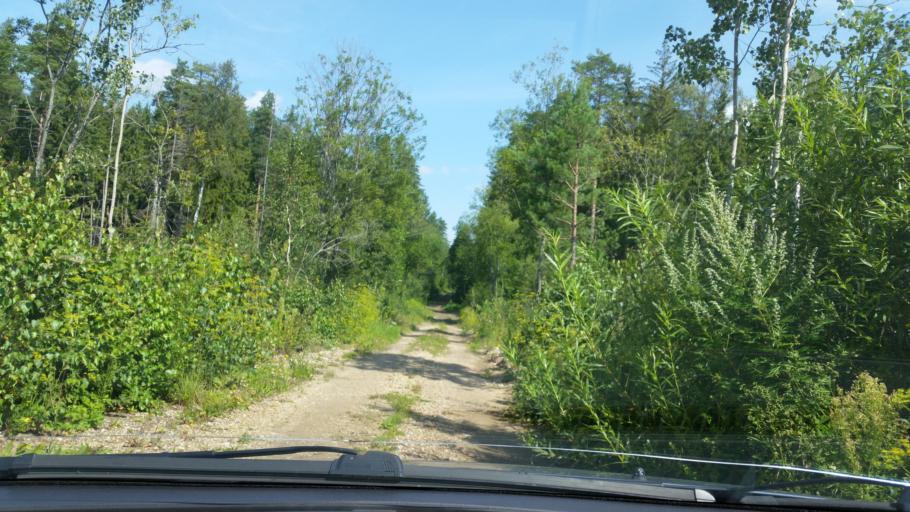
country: RU
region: Moskovskaya
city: Bol'shoye Gryzlovo
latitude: 54.8985
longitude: 37.7623
